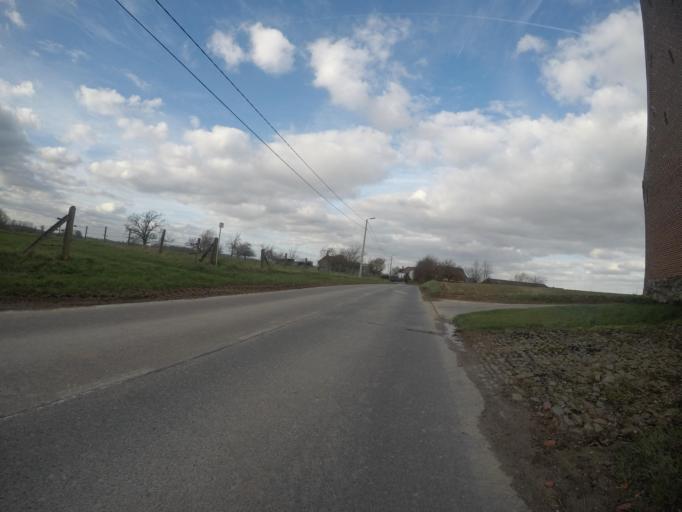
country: BE
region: Flanders
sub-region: Provincie Vlaams-Brabant
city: Pepingen
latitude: 50.7304
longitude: 4.1348
